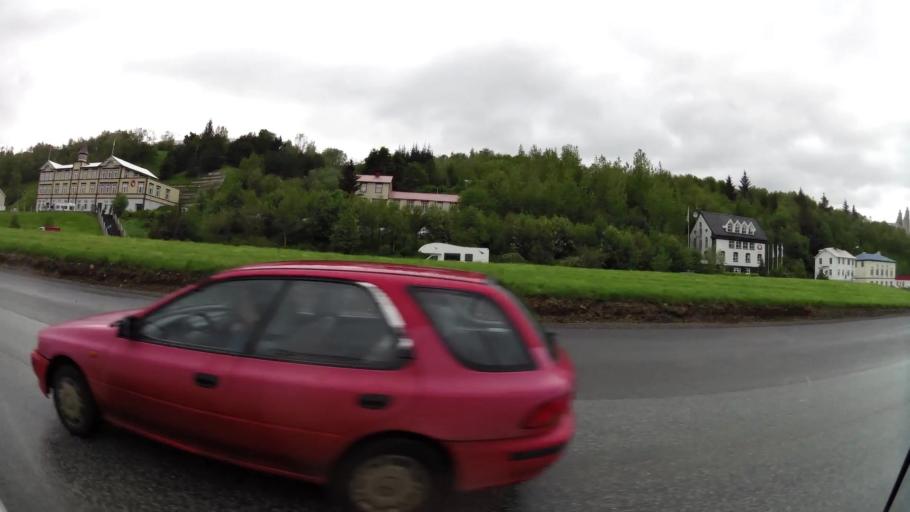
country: IS
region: Northeast
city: Akureyri
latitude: 65.6777
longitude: -18.0881
